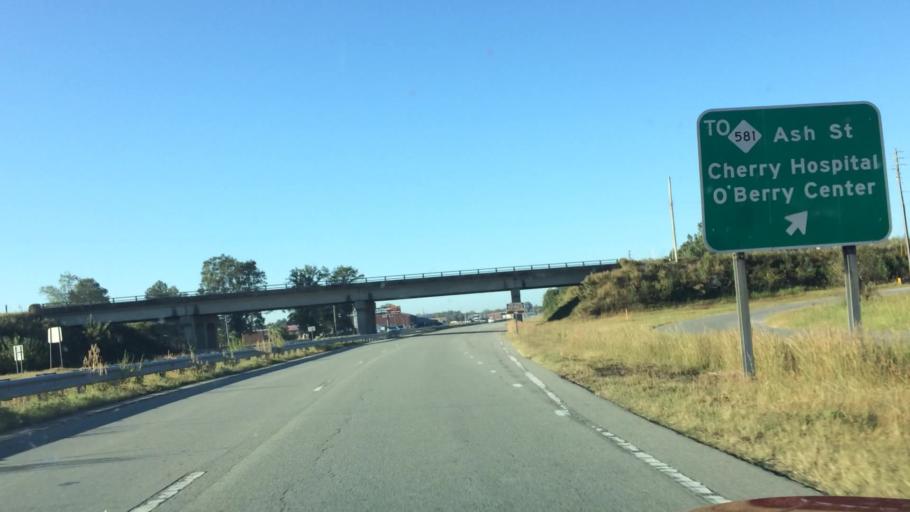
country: US
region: North Carolina
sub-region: Wayne County
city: Goldsboro
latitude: 35.3902
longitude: -78.0082
